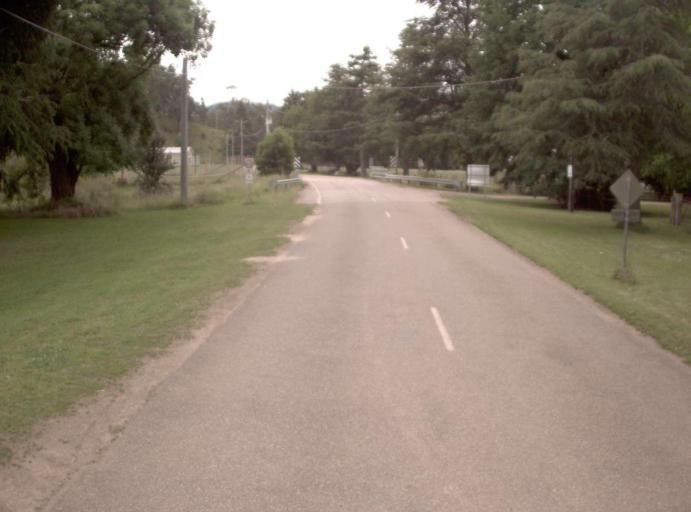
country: AU
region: Victoria
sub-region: East Gippsland
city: Bairnsdale
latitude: -37.4583
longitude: 147.2508
